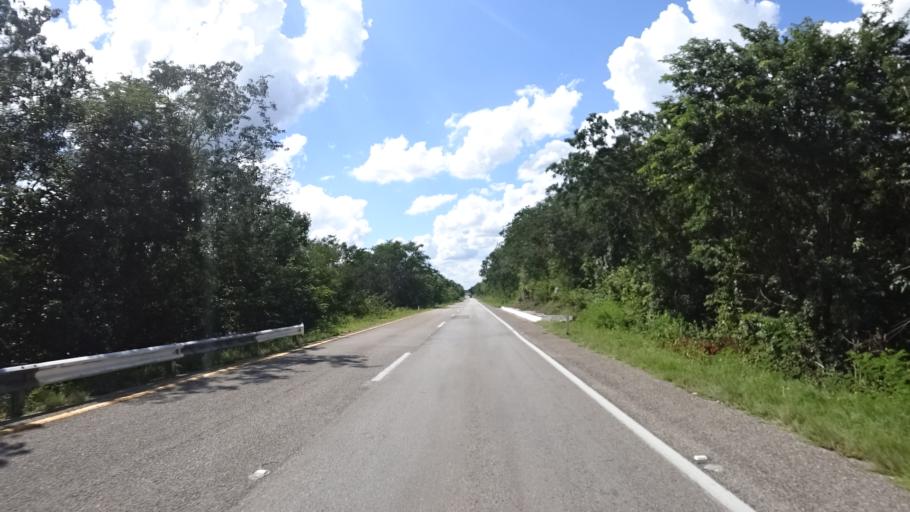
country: MX
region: Yucatan
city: Piste
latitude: 20.7333
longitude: -88.6022
